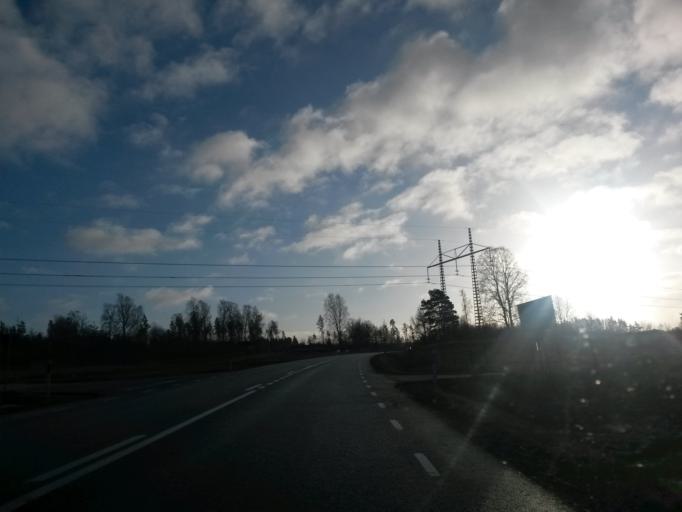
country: SE
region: Vaestra Goetaland
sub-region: Vargarda Kommun
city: Vargarda
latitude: 58.0158
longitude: 12.8172
